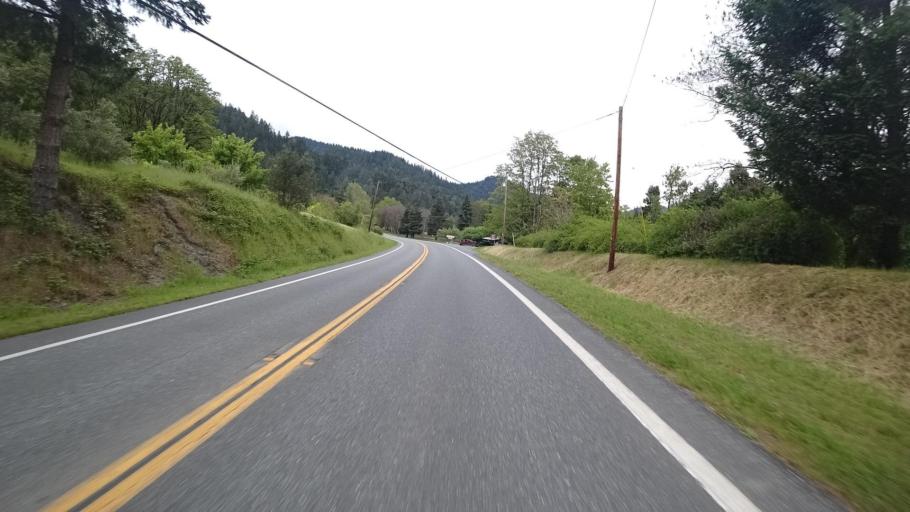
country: US
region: California
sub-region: Humboldt County
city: Willow Creek
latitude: 40.9732
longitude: -123.6395
